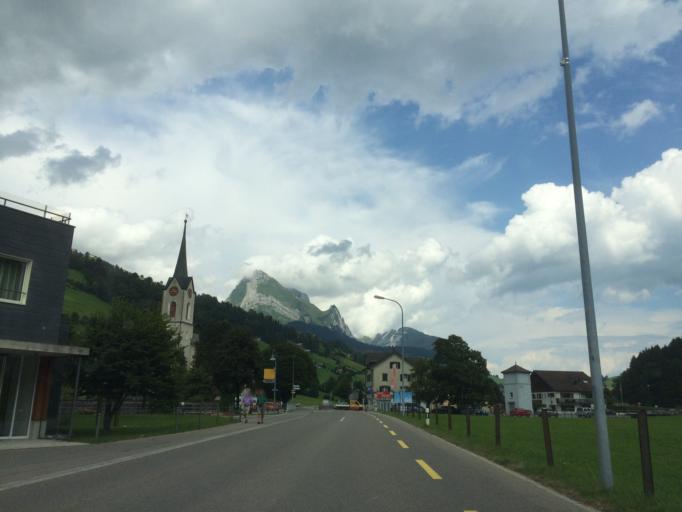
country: CH
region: Saint Gallen
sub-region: Wahlkreis Toggenburg
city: Wildhaus
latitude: 47.1935
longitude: 9.2848
